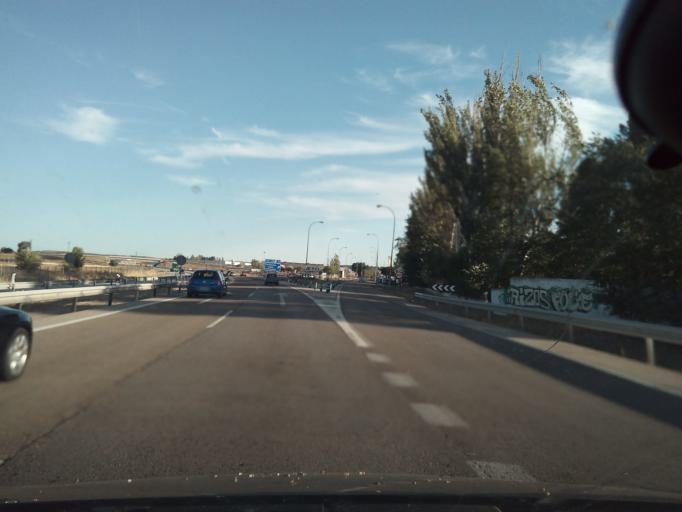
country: ES
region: Castille-La Mancha
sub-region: Province of Toledo
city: Tembleque
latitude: 39.7005
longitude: -3.4988
